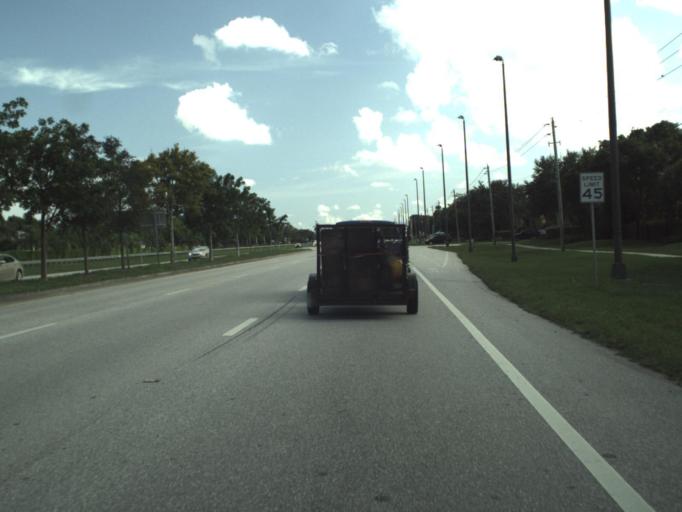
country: US
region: Florida
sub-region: Palm Beach County
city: Boca Pointe
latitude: 26.3448
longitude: -80.2034
